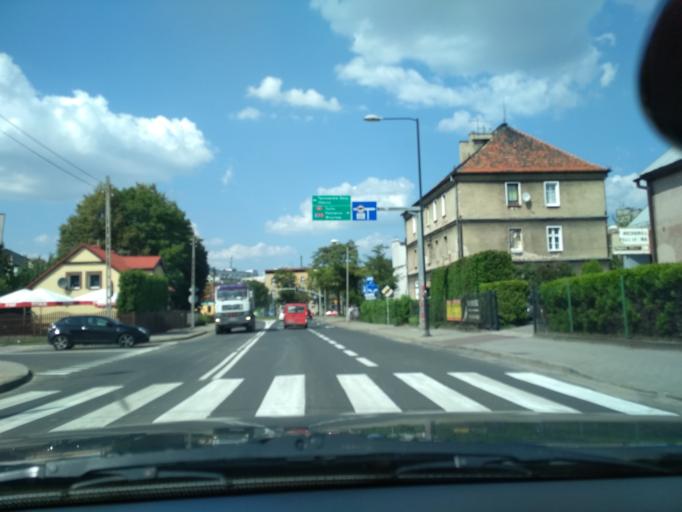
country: PL
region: Silesian Voivodeship
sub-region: Gliwice
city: Gliwice
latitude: 50.2845
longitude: 18.6756
